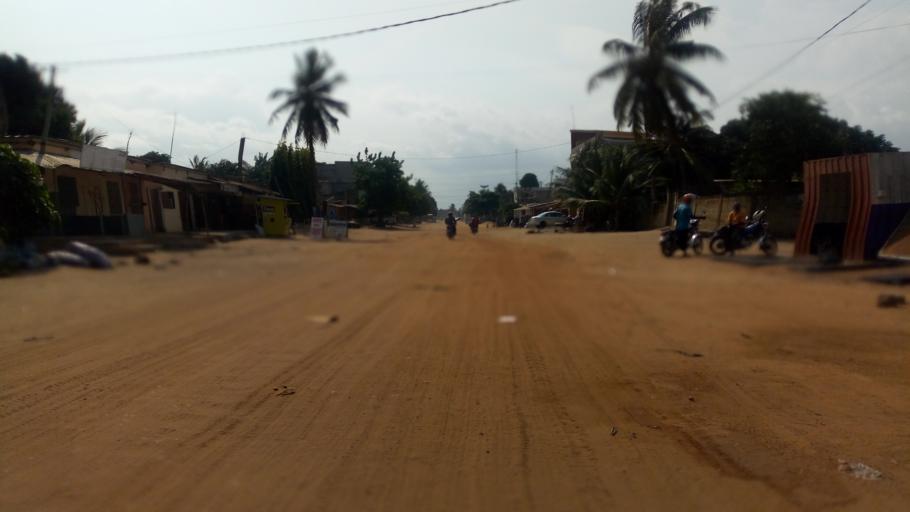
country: TG
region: Maritime
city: Lome
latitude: 6.1925
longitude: 1.1813
